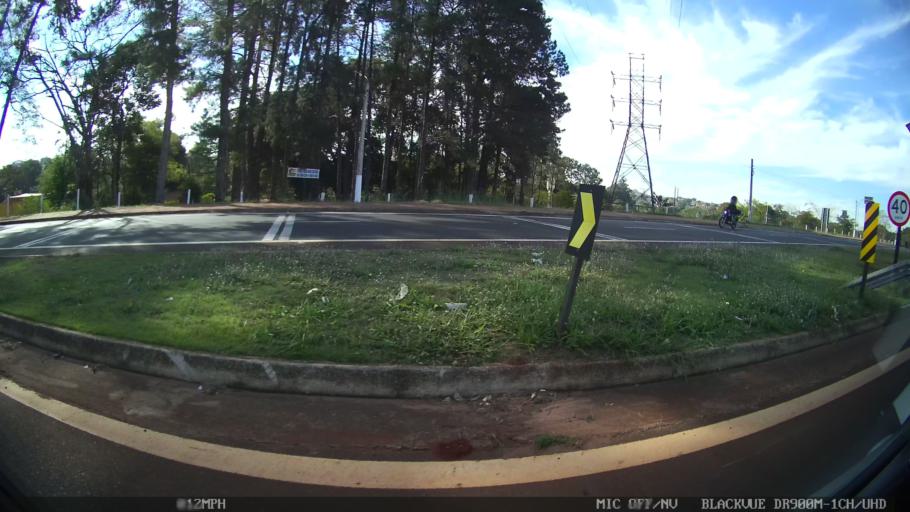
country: BR
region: Sao Paulo
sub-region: Araraquara
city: Araraquara
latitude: -21.7903
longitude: -48.1396
